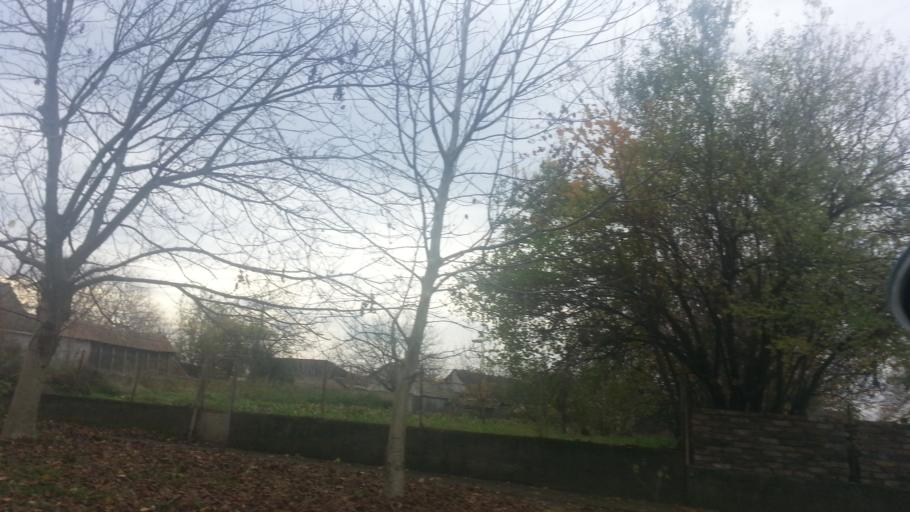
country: RS
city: Golubinci
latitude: 44.9913
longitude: 20.0678
